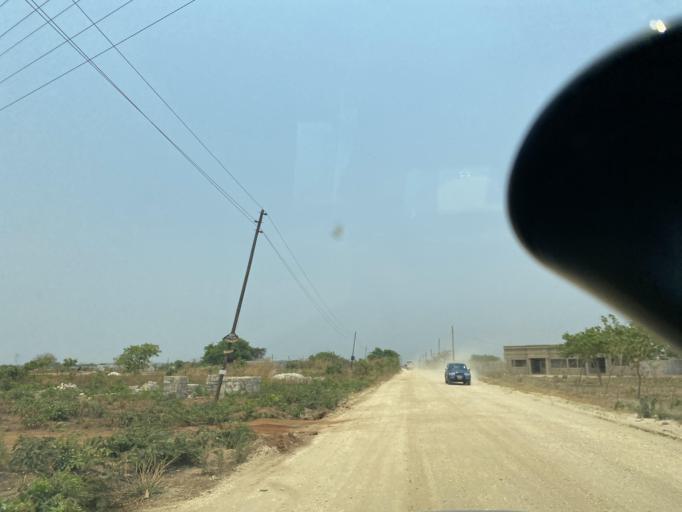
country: ZM
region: Lusaka
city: Lusaka
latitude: -15.5355
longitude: 28.3498
